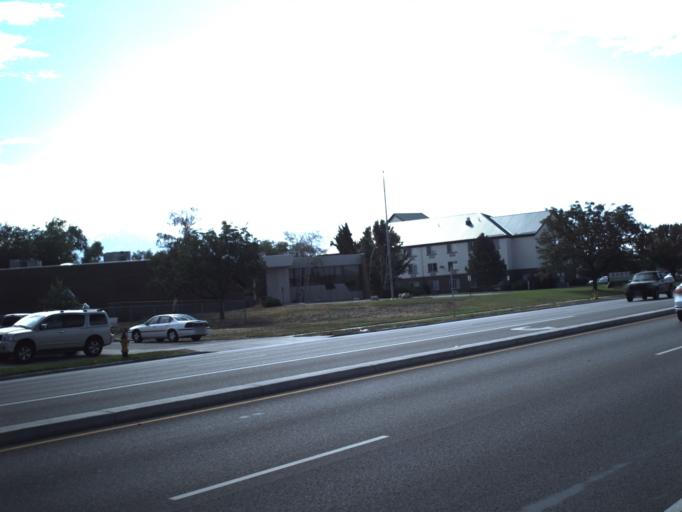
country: US
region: Utah
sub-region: Salt Lake County
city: South Salt Lake
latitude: 40.7282
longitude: -111.9392
